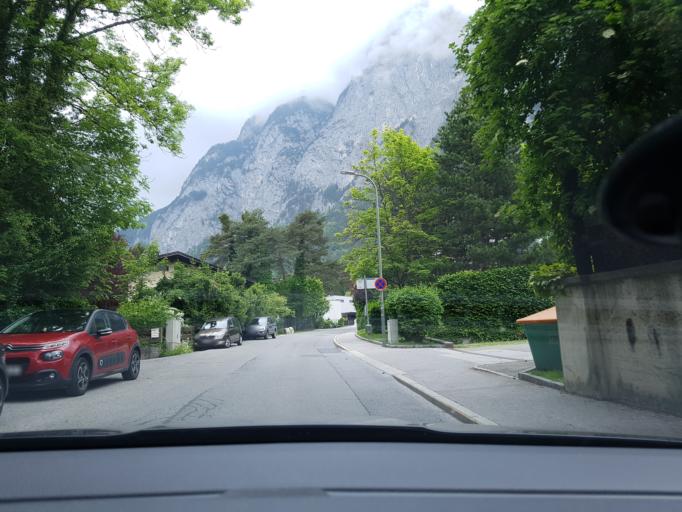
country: AT
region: Tyrol
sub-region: Politischer Bezirk Innsbruck Land
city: Vols
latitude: 47.2682
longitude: 11.3291
